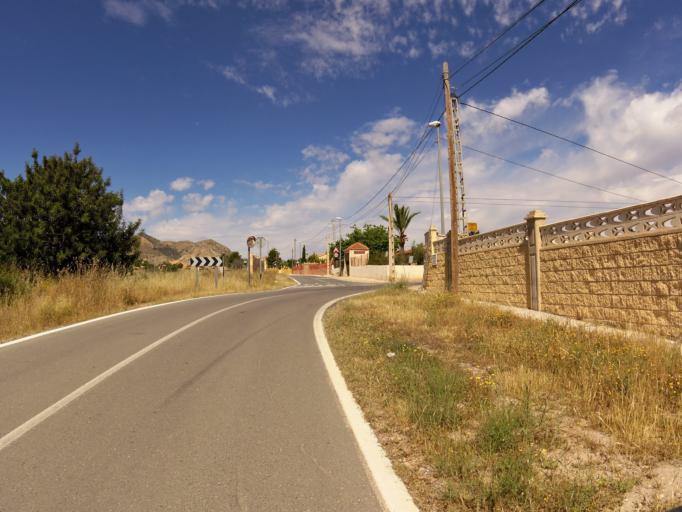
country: ES
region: Valencia
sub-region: Provincia de Alicante
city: Agost
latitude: 38.3958
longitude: -0.6010
